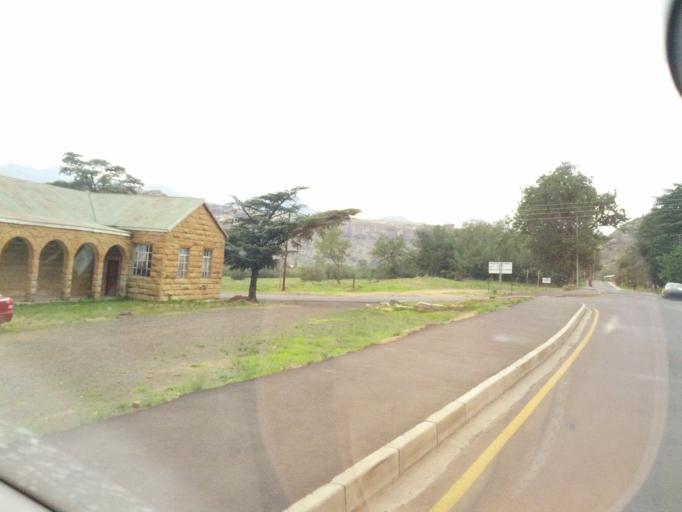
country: LS
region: Maseru
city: Nako
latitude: -29.4615
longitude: 27.7260
